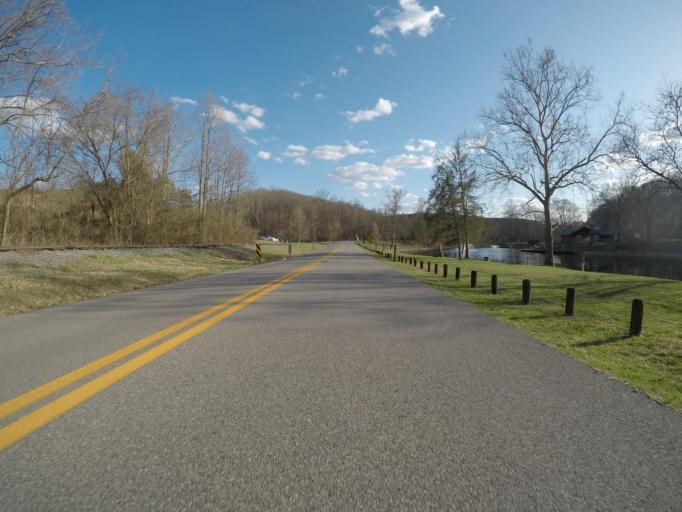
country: US
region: West Virginia
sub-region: Kanawha County
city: Charleston
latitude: 38.3912
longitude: -81.5832
